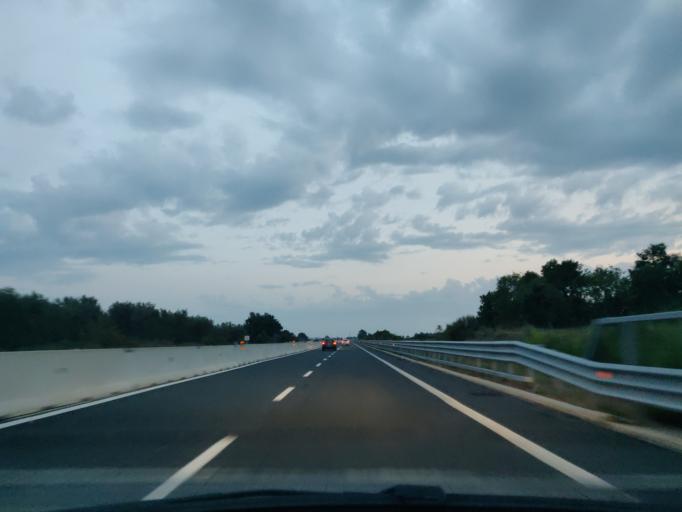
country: IT
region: Latium
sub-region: Provincia di Viterbo
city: Blera
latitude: 42.3385
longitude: 11.9833
